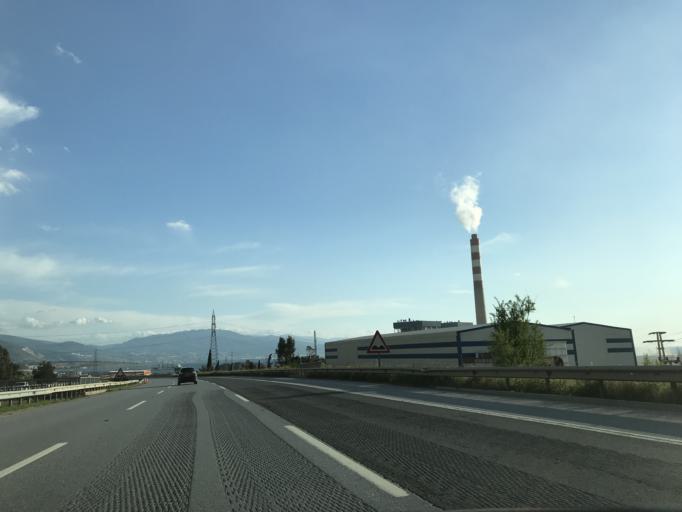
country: TR
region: Hatay
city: Denizciler
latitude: 36.6965
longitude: 36.2151
